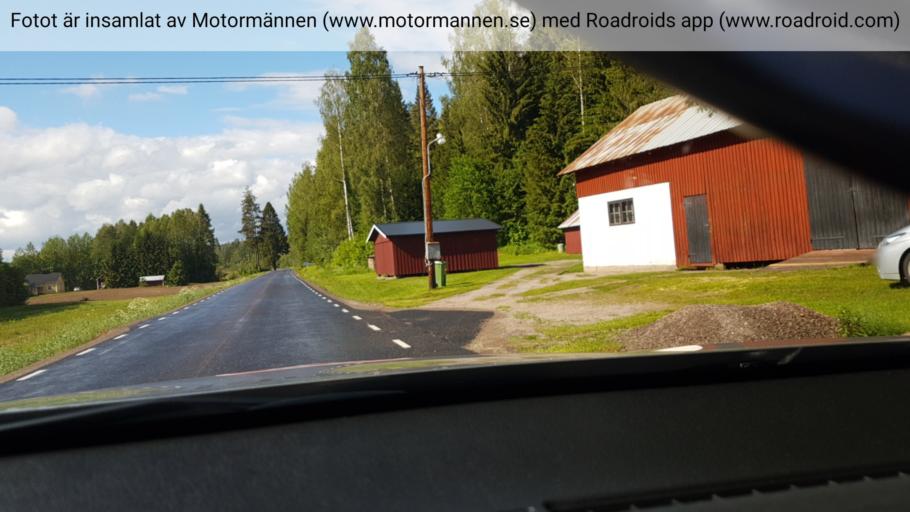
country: SE
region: Vaermland
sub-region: Hagfors Kommun
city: Ekshaerad
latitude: 60.2545
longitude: 13.4679
